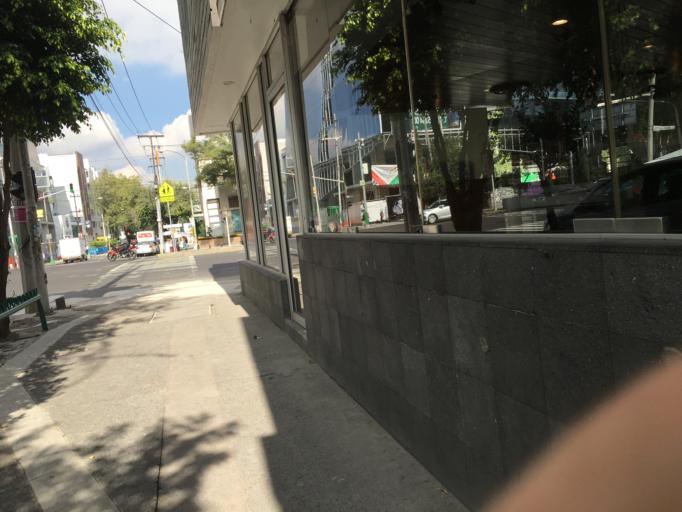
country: MX
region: Mexico City
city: Colonia del Valle
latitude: 19.3746
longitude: -99.1619
